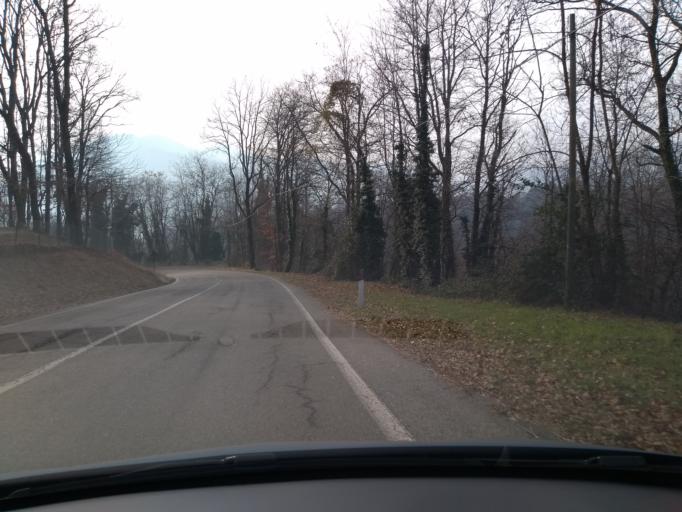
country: IT
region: Piedmont
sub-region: Provincia di Torino
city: Balangero
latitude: 45.2827
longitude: 7.5041
